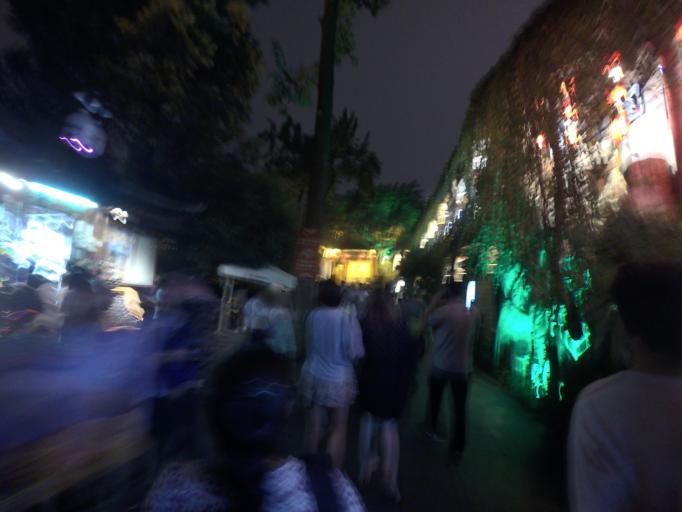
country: CN
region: Sichuan
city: Chengdu
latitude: 30.6484
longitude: 104.0475
